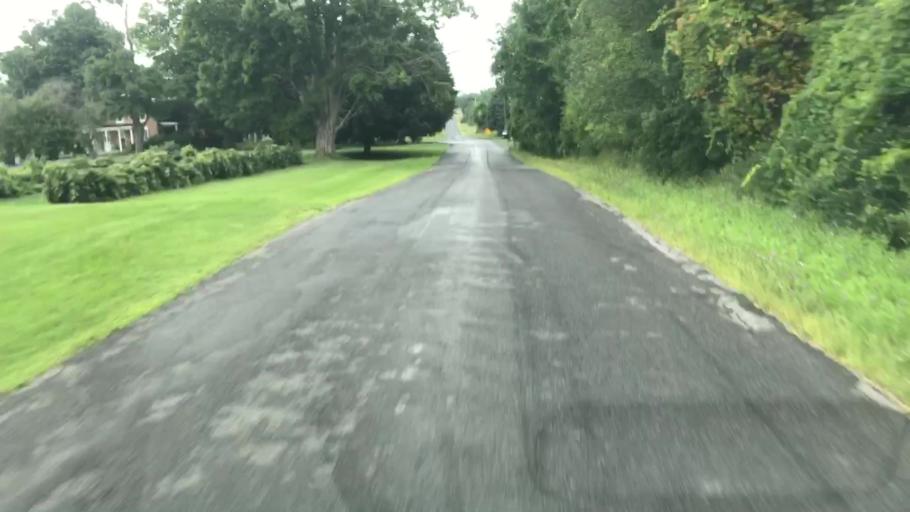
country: US
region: New York
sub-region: Cayuga County
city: Melrose Park
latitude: 42.9697
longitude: -76.5078
